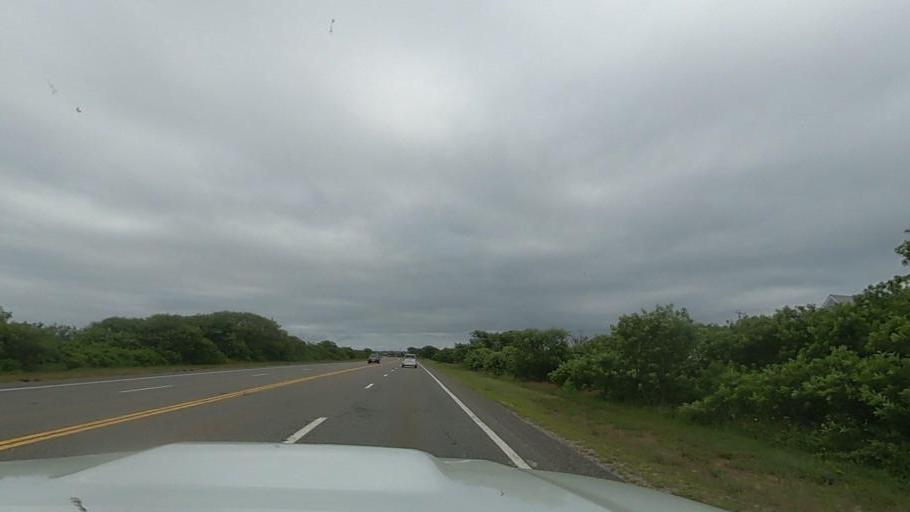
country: US
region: Massachusetts
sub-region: Barnstable County
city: Provincetown
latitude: 42.0598
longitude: -70.1394
